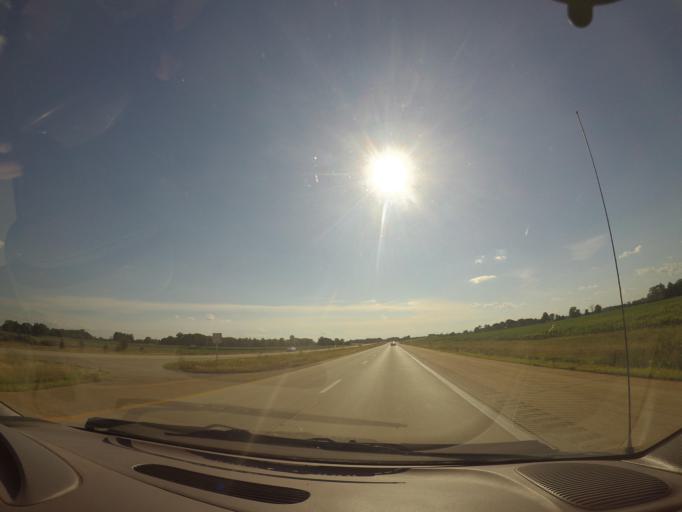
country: US
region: Ohio
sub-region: Lucas County
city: Whitehouse
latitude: 41.4561
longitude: -83.8151
